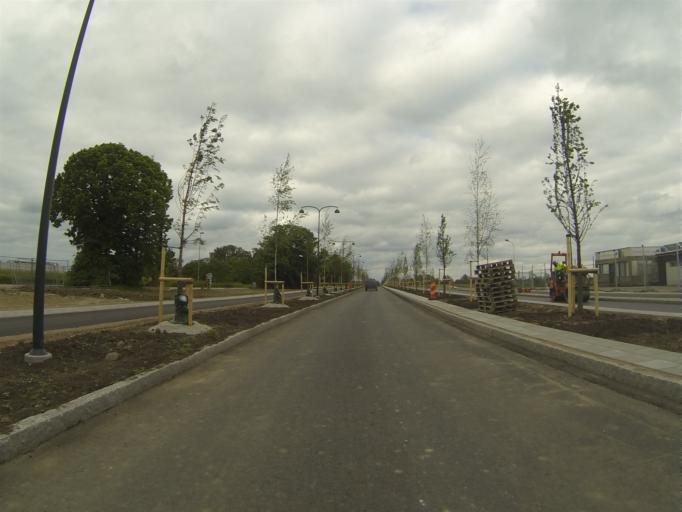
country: SE
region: Skane
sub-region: Lunds Kommun
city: Lund
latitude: 55.7232
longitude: 13.2301
